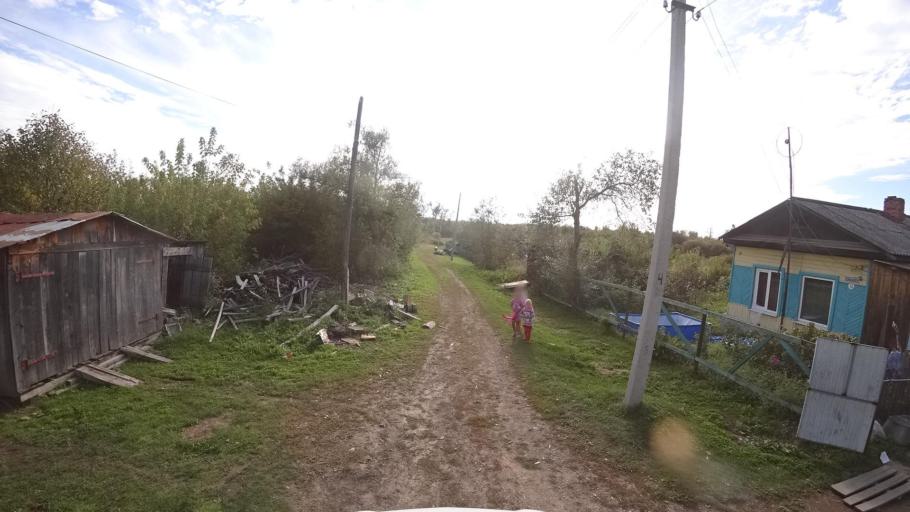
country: RU
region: Primorskiy
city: Dostoyevka
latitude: 44.3073
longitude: 133.4654
